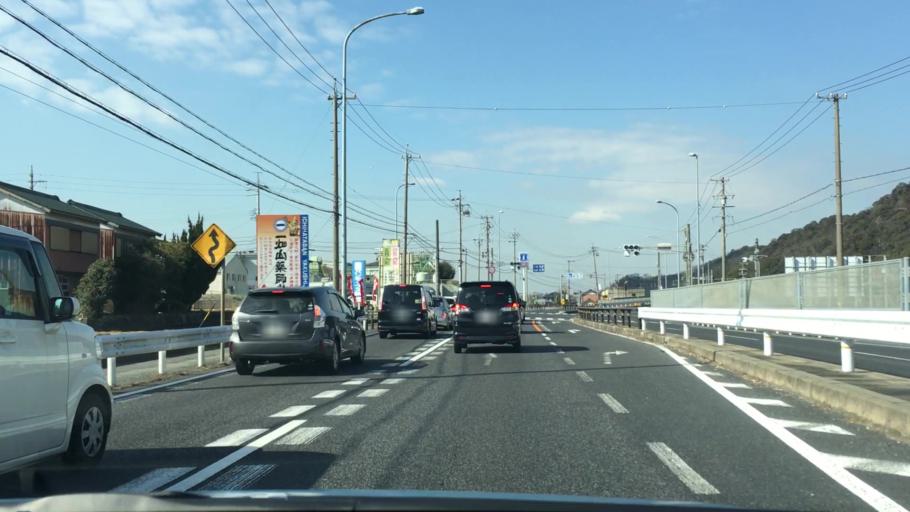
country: JP
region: Aichi
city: Gamagori
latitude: 34.9068
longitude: 137.2316
